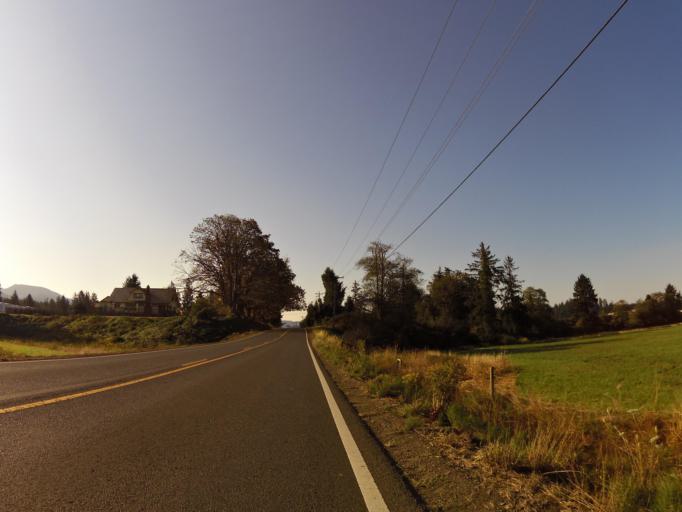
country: US
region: Oregon
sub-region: Tillamook County
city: Tillamook
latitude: 45.4322
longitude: -123.7777
